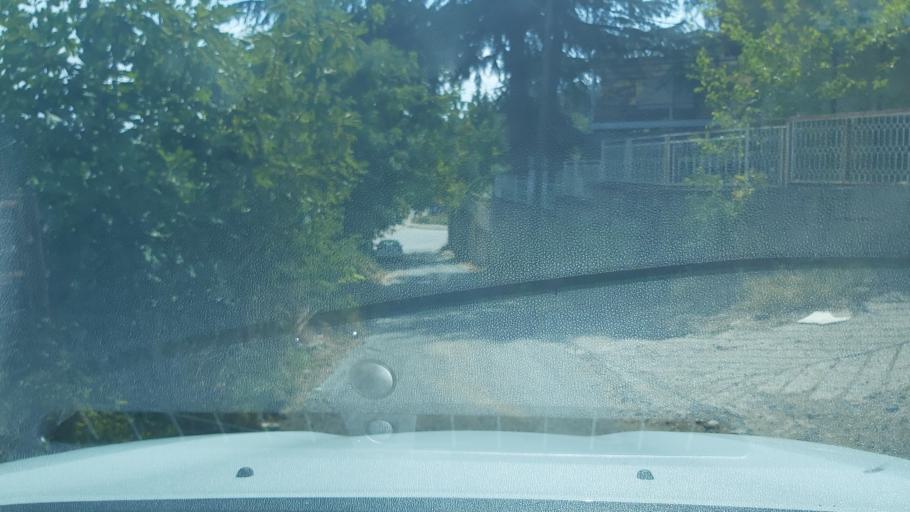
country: MK
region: Dojran
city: Star Dojran
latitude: 41.1796
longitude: 22.7239
